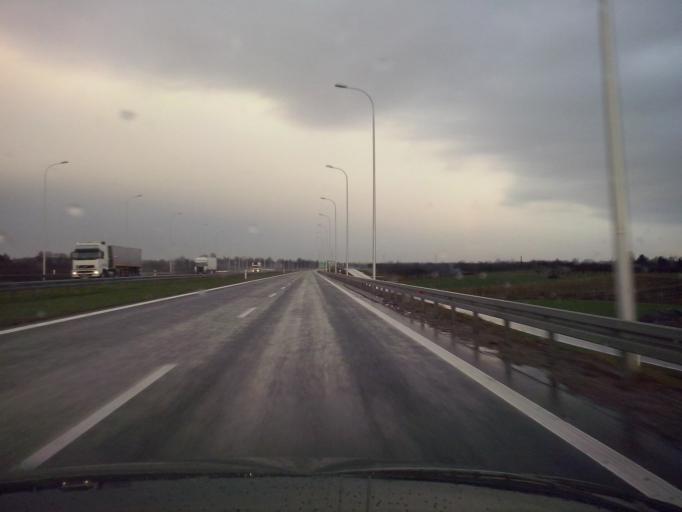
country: PL
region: Lublin Voivodeship
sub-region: Powiat lubelski
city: Jastkow
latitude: 51.2796
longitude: 22.4648
